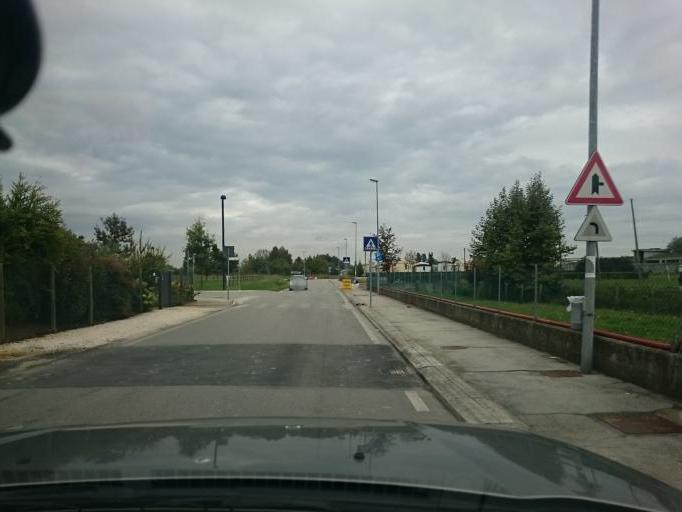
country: IT
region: Veneto
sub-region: Provincia di Padova
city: Vallonga
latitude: 45.2746
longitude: 12.0763
